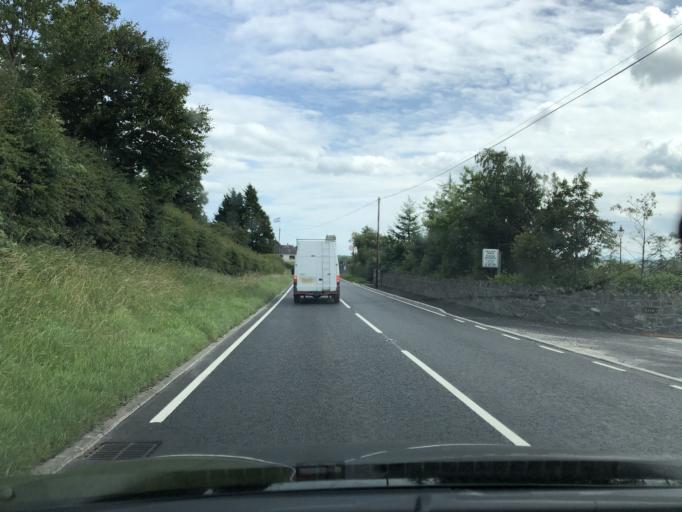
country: GB
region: Northern Ireland
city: Ballynahinch
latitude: 54.4313
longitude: -5.9305
